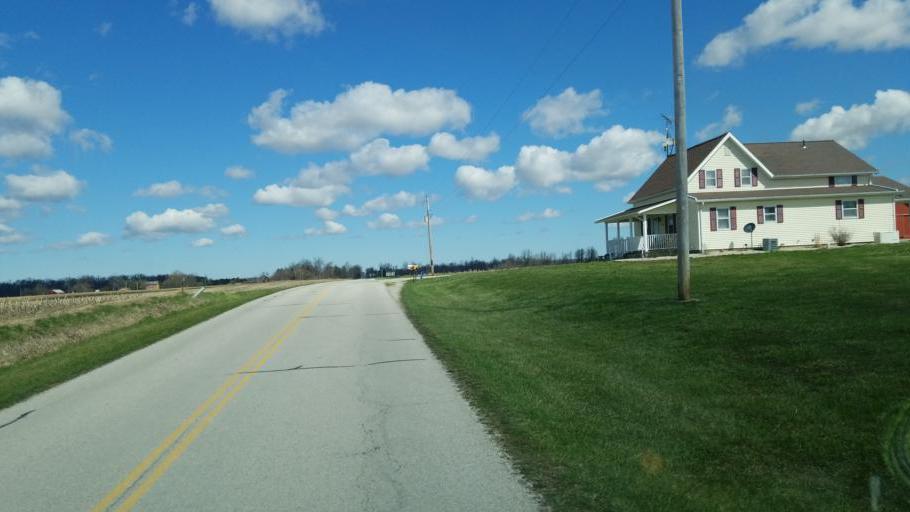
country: US
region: Ohio
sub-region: Sandusky County
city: Mount Carmel
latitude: 41.1557
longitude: -82.9381
